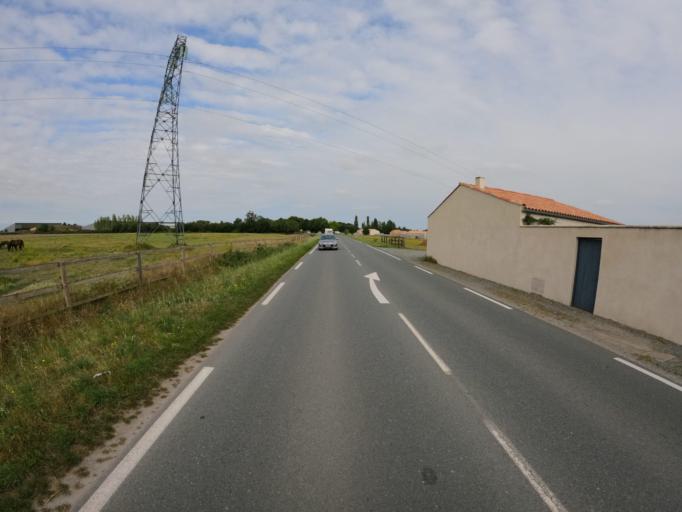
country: FR
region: Pays de la Loire
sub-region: Departement de la Vendee
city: Champagne-les-Marais
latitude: 46.3779
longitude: -1.1101
